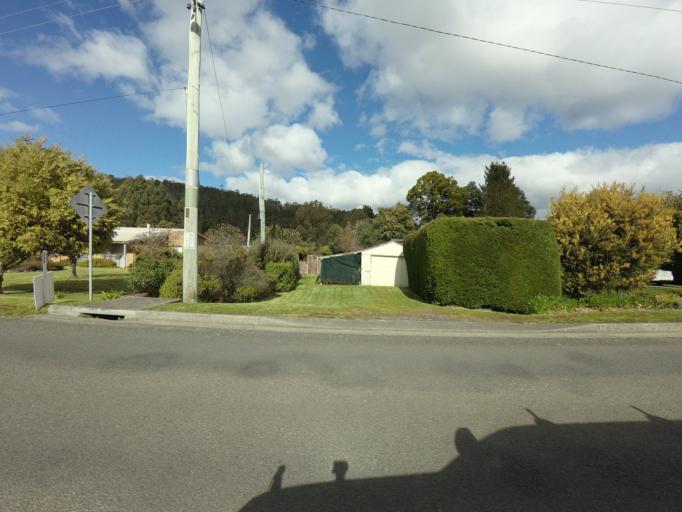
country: AU
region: Tasmania
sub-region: Huon Valley
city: Geeveston
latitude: -43.1711
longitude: 146.9245
